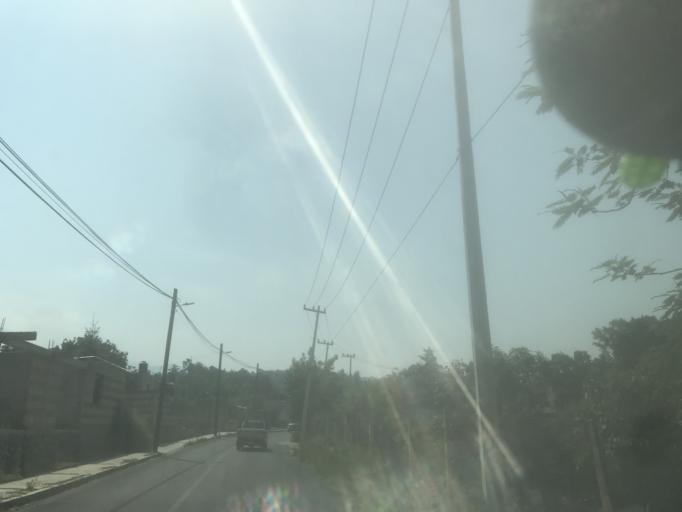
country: MX
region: Mexico
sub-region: Atlautla
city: San Juan Tepecoculco
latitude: 18.9918
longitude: -98.7929
